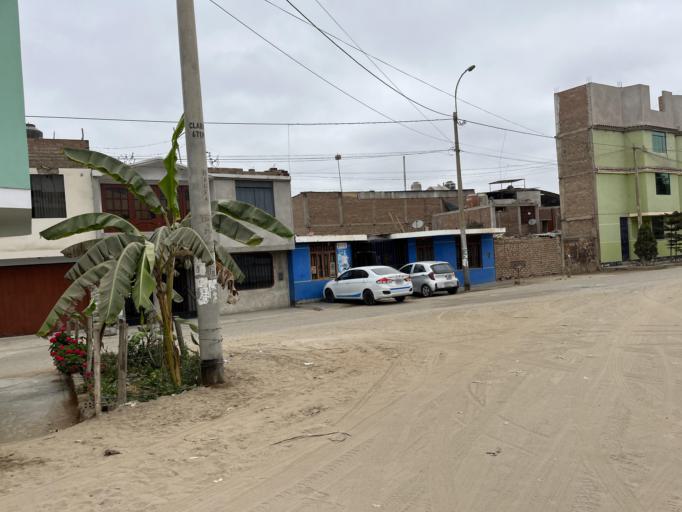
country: PE
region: La Libertad
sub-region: Provincia de Trujillo
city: La Esperanza
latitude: -8.0884
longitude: -79.0372
